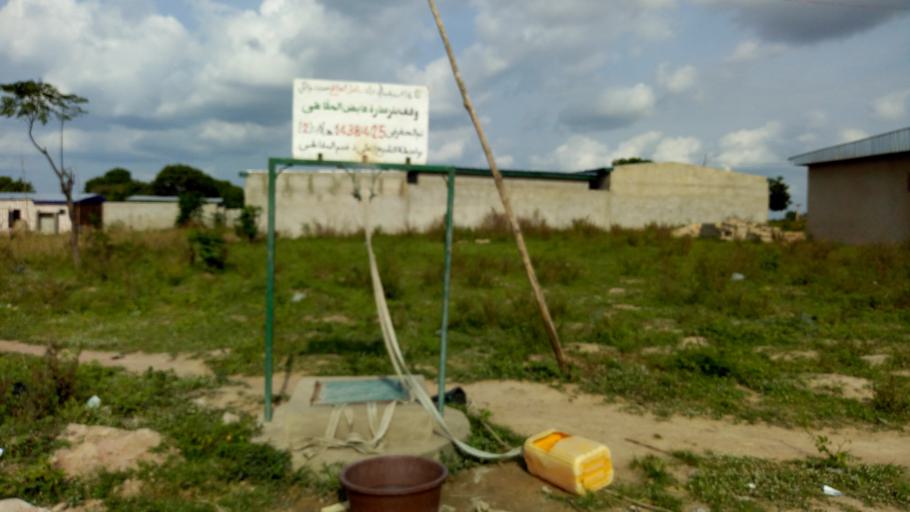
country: CI
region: Vallee du Bandama
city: Bouake
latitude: 7.7319
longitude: -5.0140
